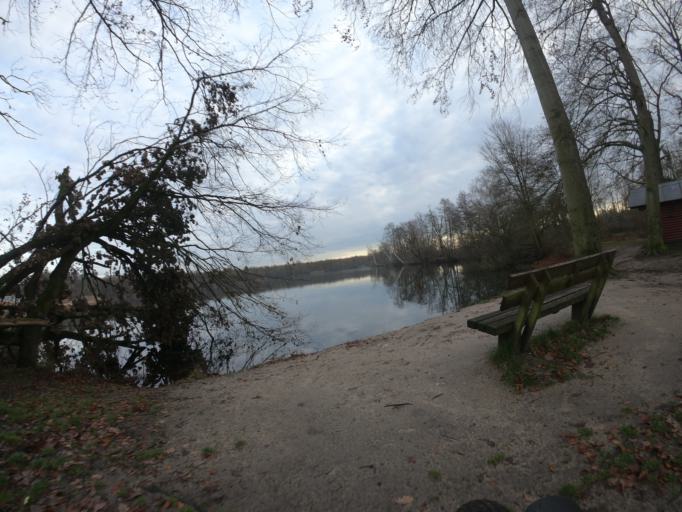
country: DE
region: Hesse
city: Morfelden-Walldorf
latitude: 49.9692
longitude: 8.5942
